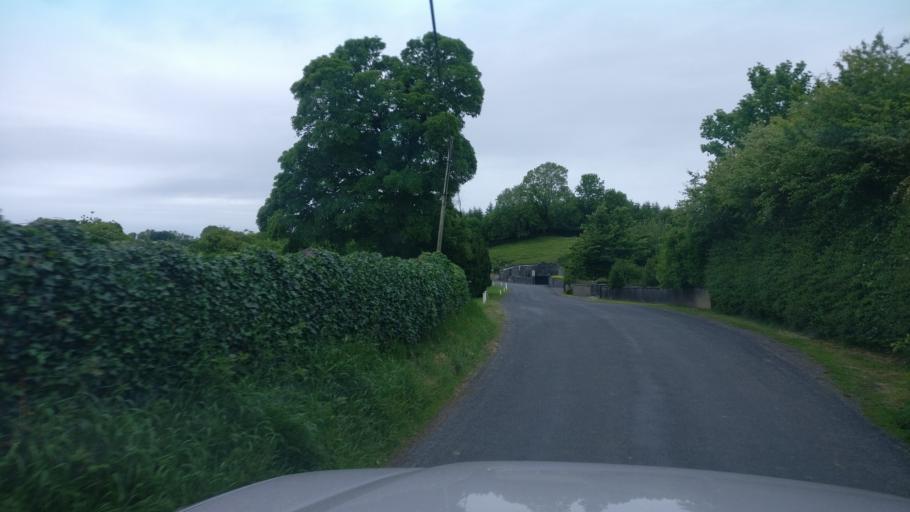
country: IE
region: Connaught
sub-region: County Galway
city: Portumna
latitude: 53.1094
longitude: -8.4025
